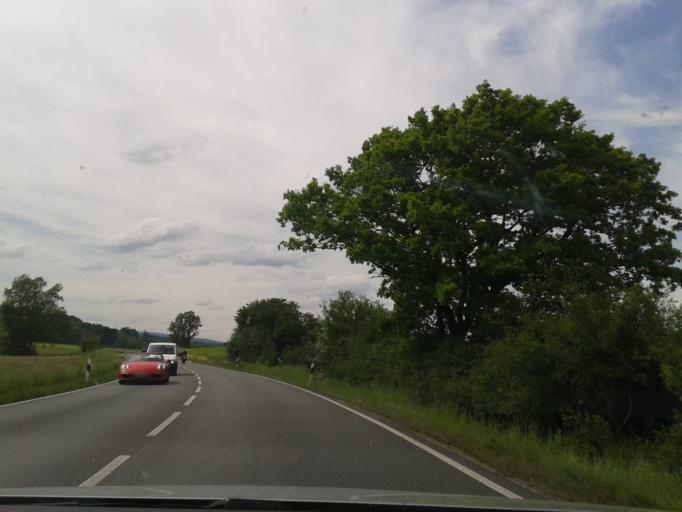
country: DE
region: Hesse
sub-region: Regierungsbezirk Giessen
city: Colbe
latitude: 50.8803
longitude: 8.7663
